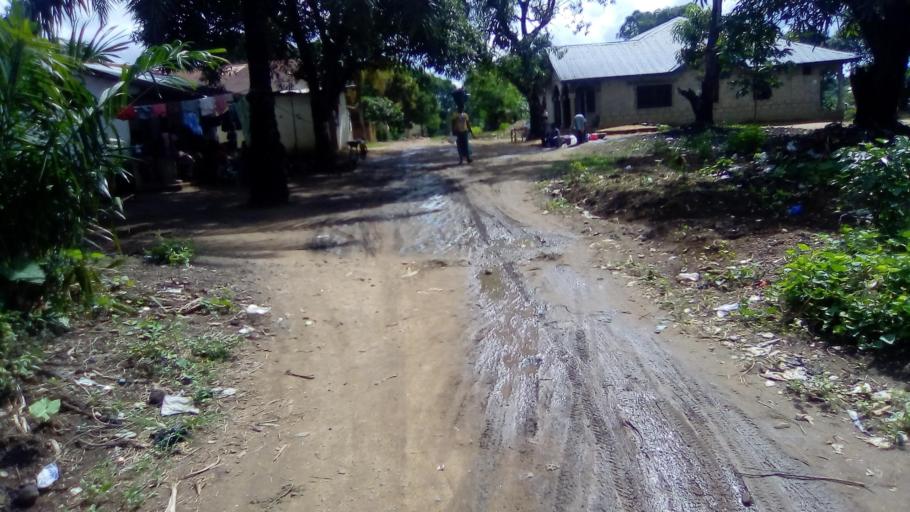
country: SL
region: Southern Province
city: Bo
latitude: 7.9786
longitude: -11.7265
